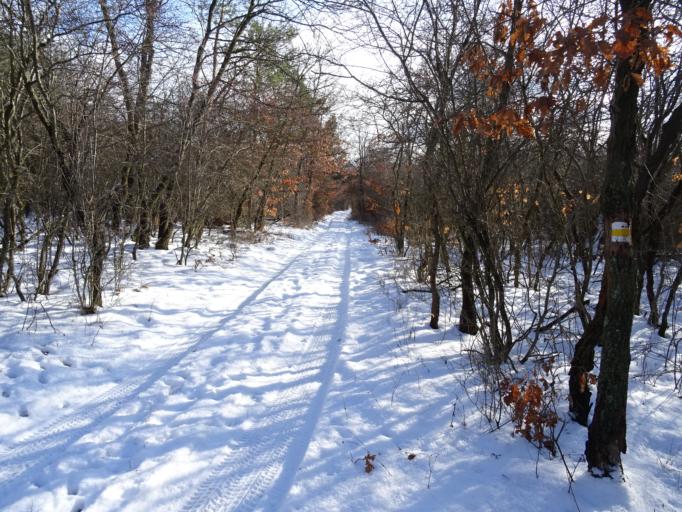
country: HU
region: Komarom-Esztergom
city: Oroszlany
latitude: 47.4782
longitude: 18.3670
